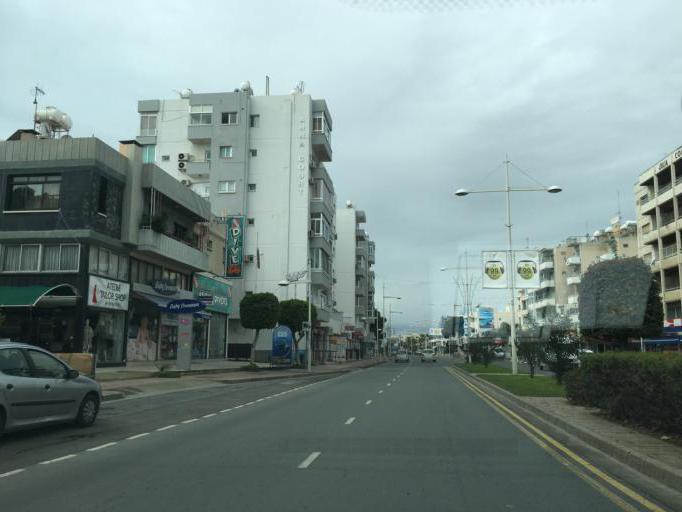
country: CY
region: Limassol
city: Mouttagiaka
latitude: 34.6928
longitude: 33.0812
